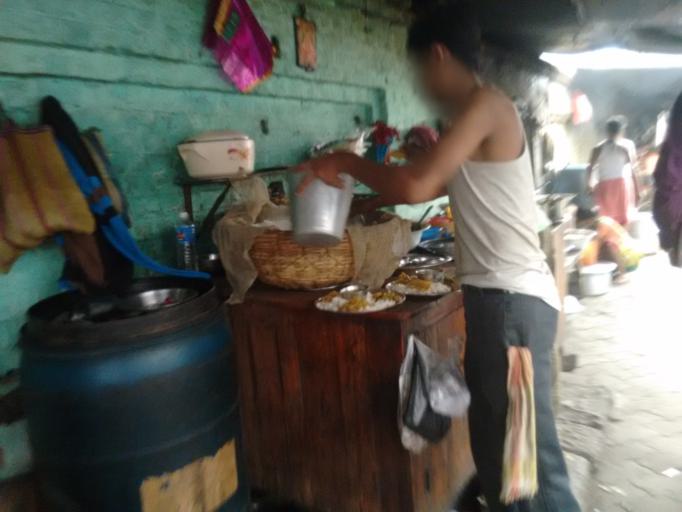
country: IN
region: West Bengal
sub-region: Kolkata
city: Kolkata
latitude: 22.5656
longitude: 88.3694
